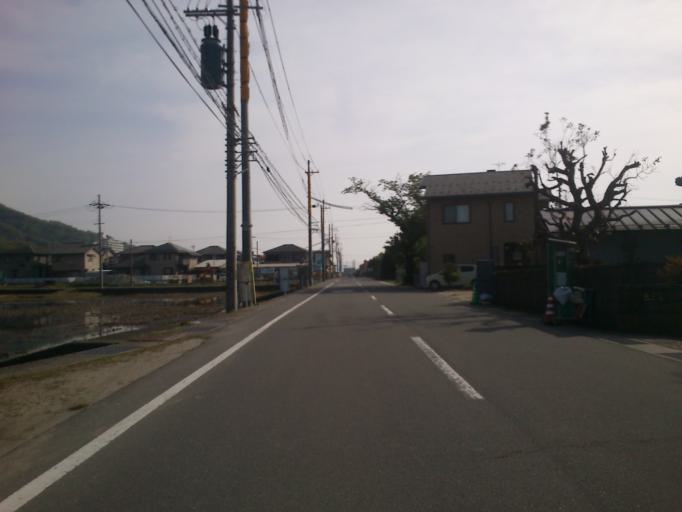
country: JP
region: Kyoto
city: Miyazu
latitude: 35.5812
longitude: 135.2013
